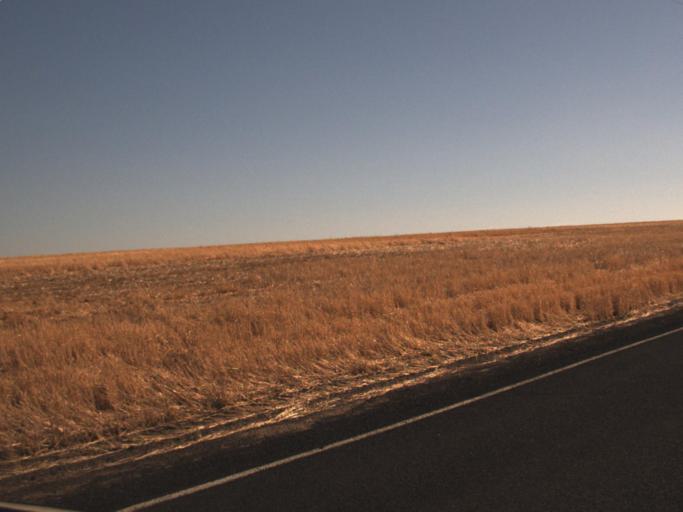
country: US
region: Washington
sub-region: Adams County
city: Ritzville
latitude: 46.9292
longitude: -118.5671
